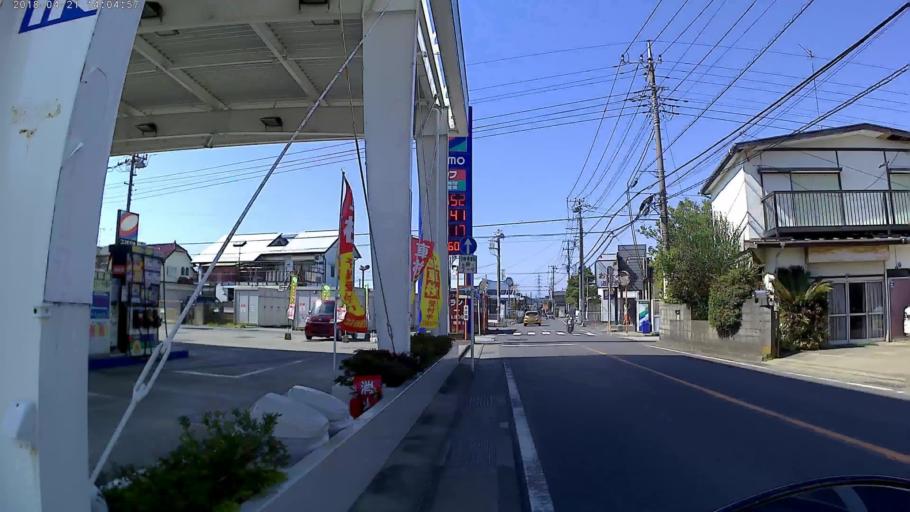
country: JP
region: Kanagawa
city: Hiratsuka
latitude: 35.3528
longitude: 139.3500
